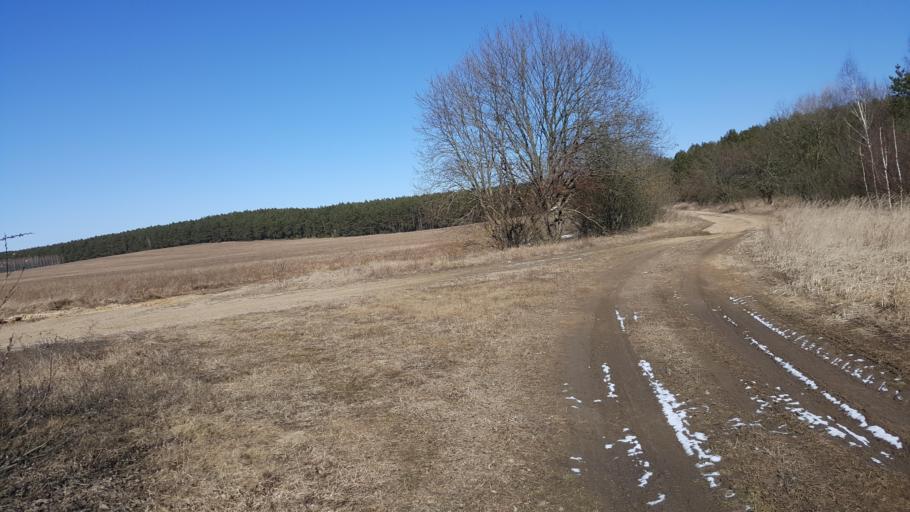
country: BY
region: Brest
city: Kamyanyets
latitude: 52.3762
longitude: 23.8383
